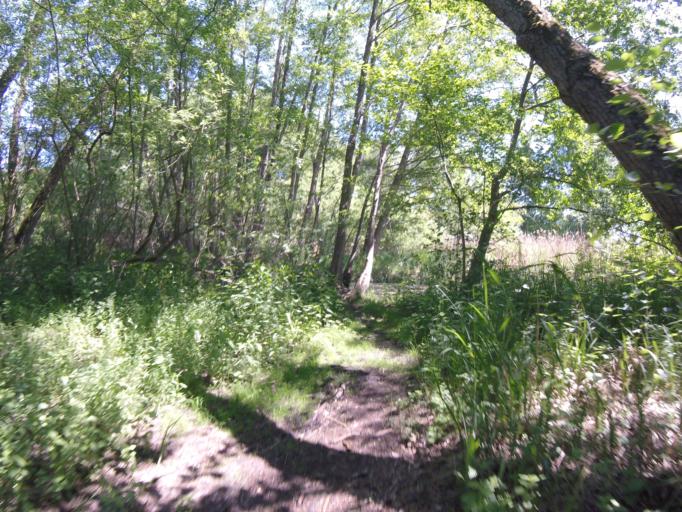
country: DE
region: Brandenburg
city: Bestensee
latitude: 52.2412
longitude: 13.6765
